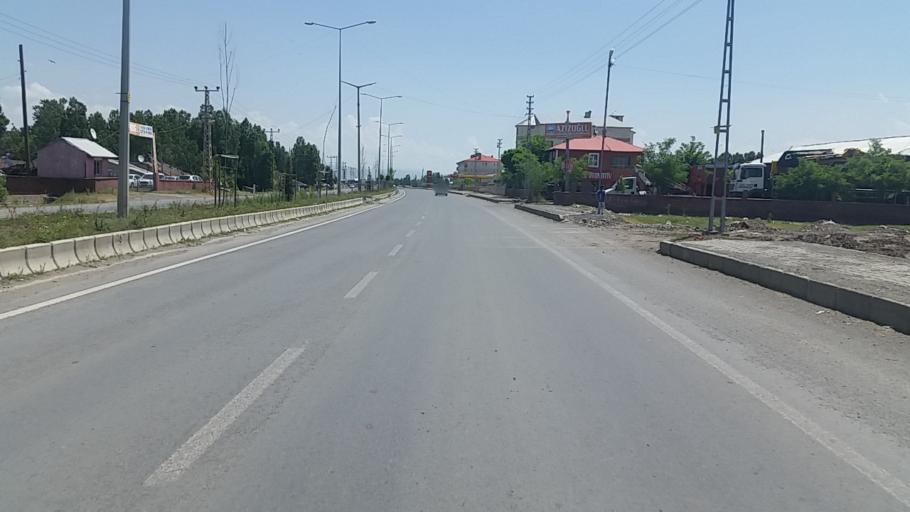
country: TR
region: Agri
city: Agri
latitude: 39.7078
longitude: 43.0528
